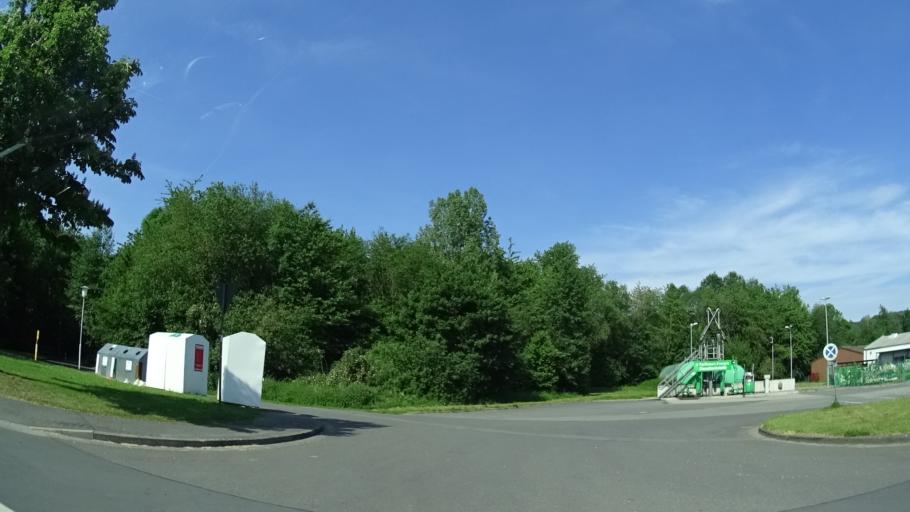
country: DE
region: Hesse
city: Michelstadt
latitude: 49.6855
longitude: 8.9991
